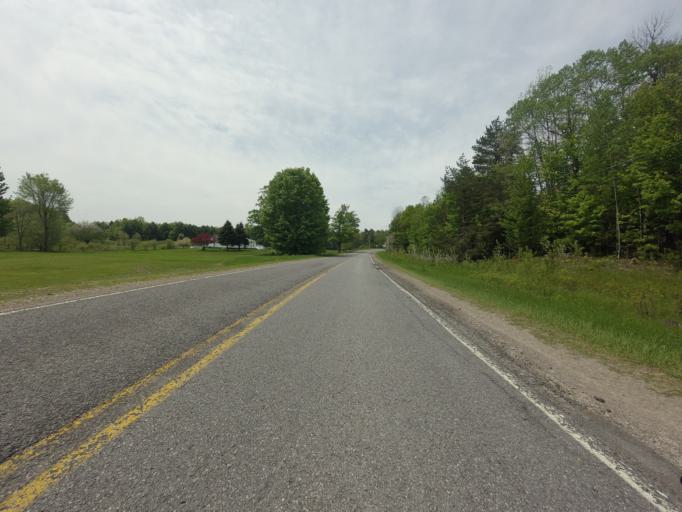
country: US
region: New York
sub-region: St. Lawrence County
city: Hannawa Falls
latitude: 44.6113
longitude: -74.8776
